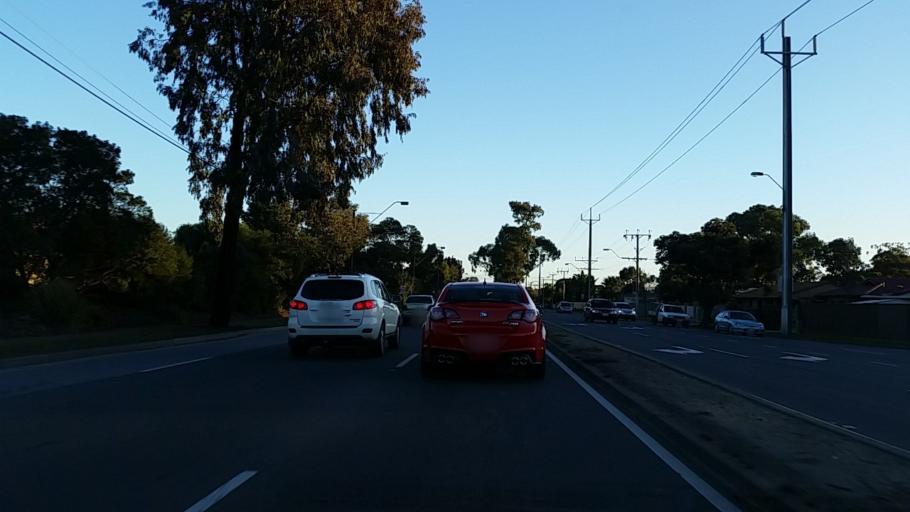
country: AU
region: South Australia
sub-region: Salisbury
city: Salisbury
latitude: -34.7795
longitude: 138.6261
